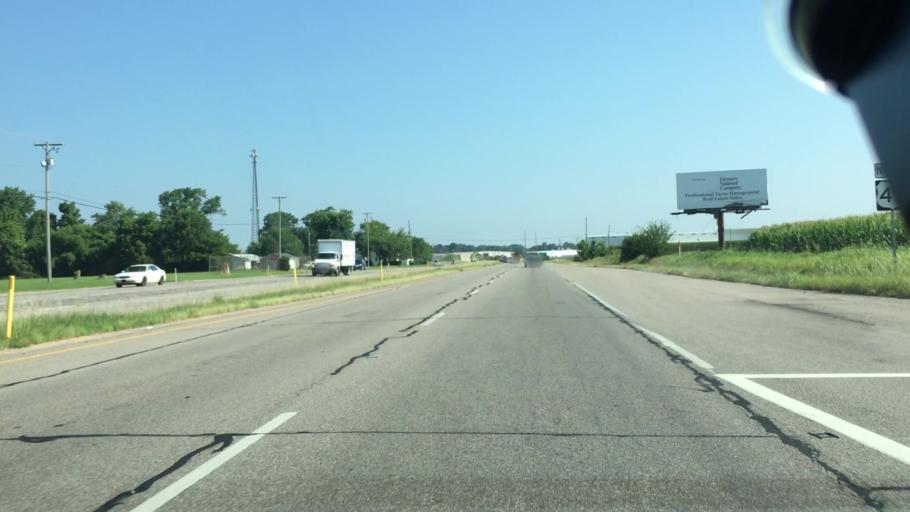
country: US
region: Indiana
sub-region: Gibson County
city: Princeton
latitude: 38.3048
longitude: -87.5673
